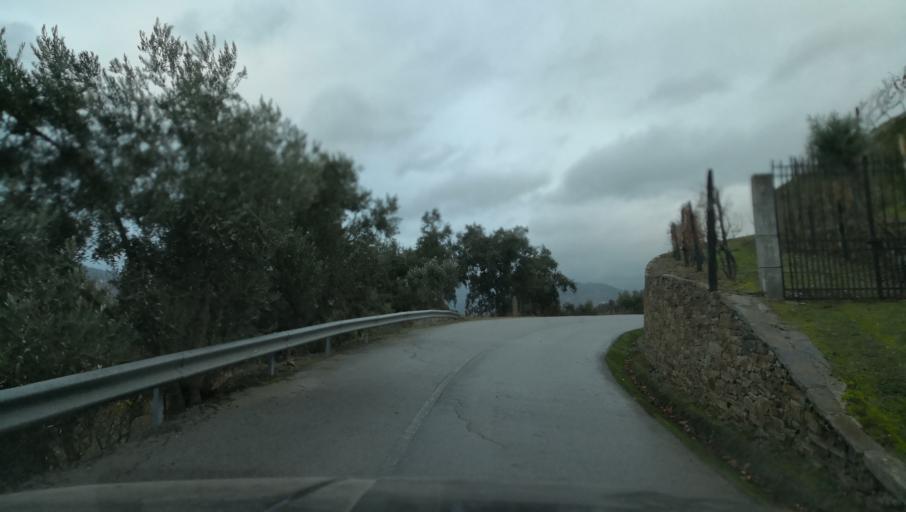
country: PT
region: Vila Real
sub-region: Santa Marta de Penaguiao
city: Santa Marta de Penaguiao
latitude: 41.2062
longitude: -7.7551
